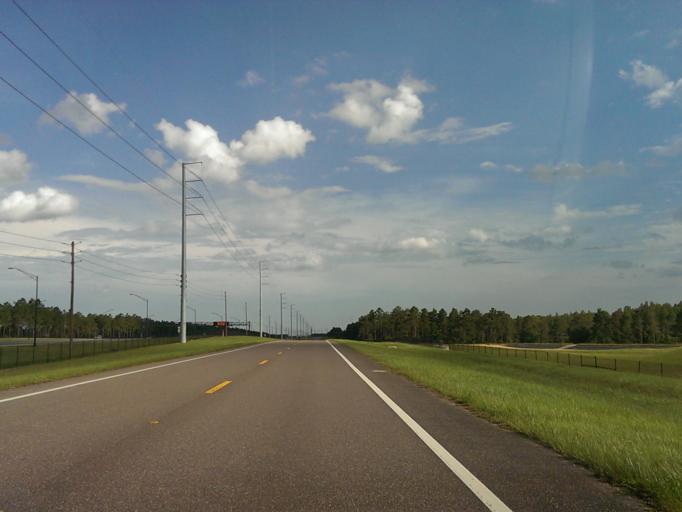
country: US
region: Florida
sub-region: Polk County
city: Citrus Ridge
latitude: 28.4092
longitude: -81.6278
